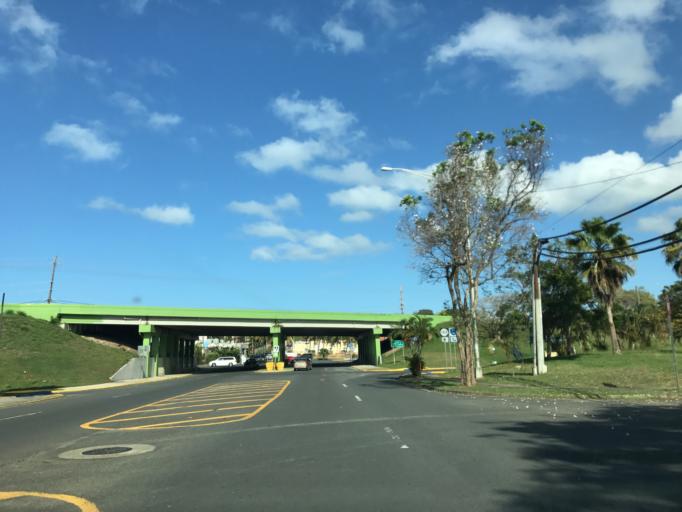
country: PR
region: Luquillo
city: Luquillo
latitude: 18.3716
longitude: -65.7170
